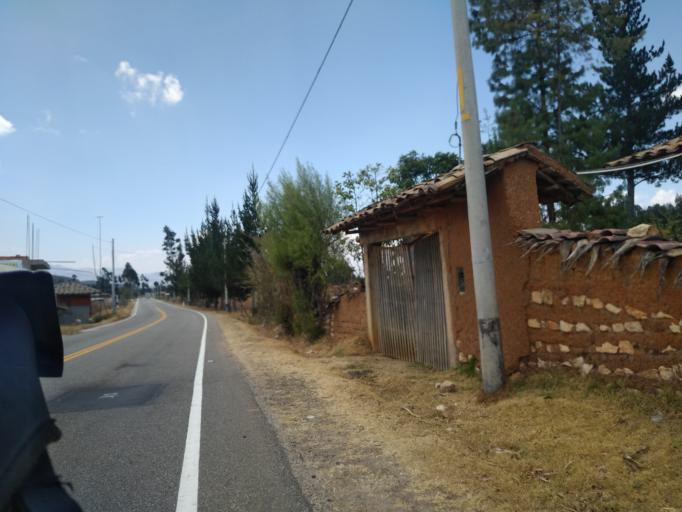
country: PE
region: Cajamarca
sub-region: San Marcos
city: San Marcos
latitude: -7.2809
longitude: -78.2305
